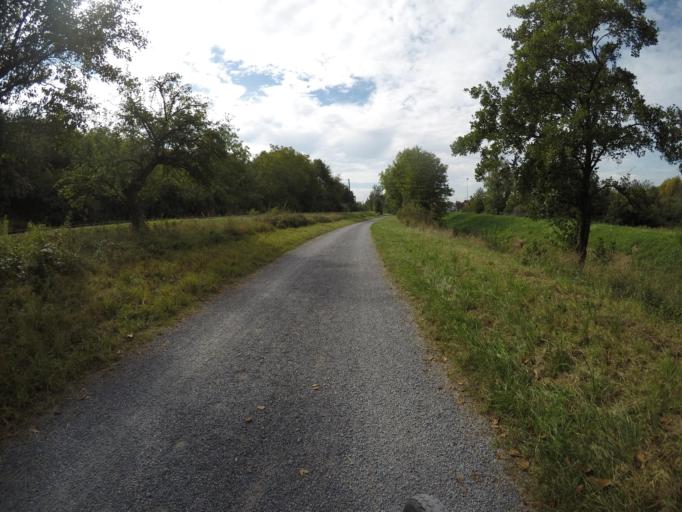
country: DE
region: Baden-Wuerttemberg
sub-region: Karlsruhe Region
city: Ubstadt-Weiher
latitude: 49.1675
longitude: 8.6317
